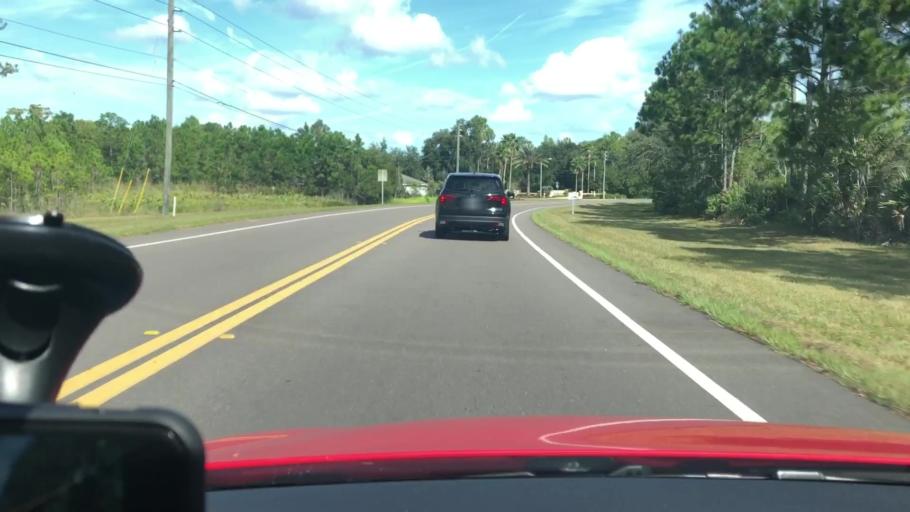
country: US
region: Florida
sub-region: Volusia County
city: Ormond Beach
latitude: 29.2590
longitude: -81.0985
